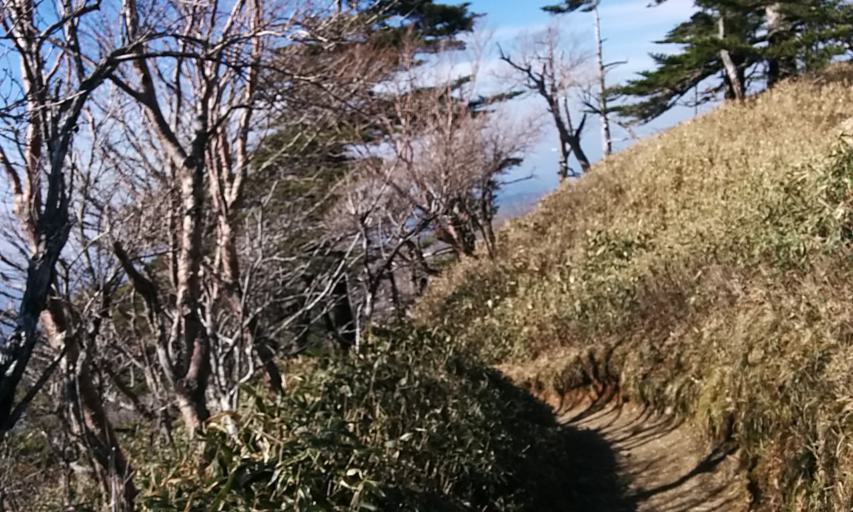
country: JP
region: Tokushima
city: Wakimachi
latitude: 33.8570
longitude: 134.0954
